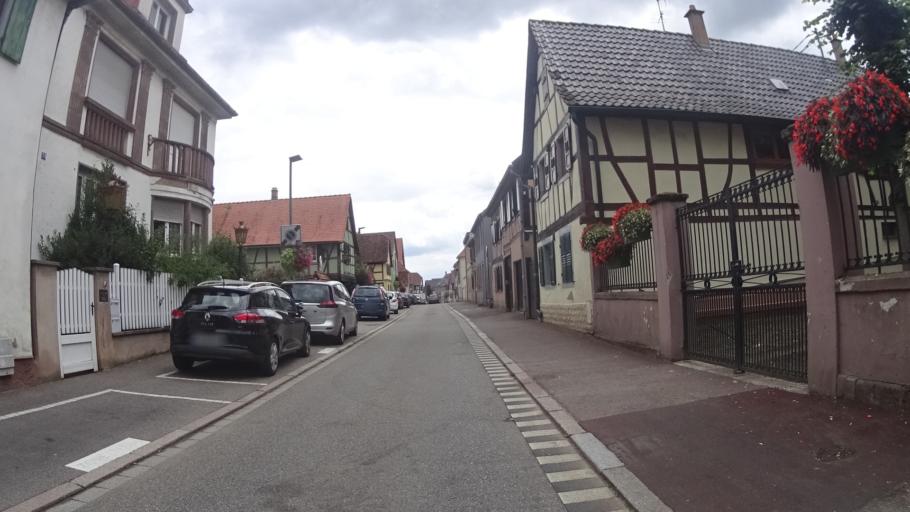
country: FR
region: Alsace
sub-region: Departement du Bas-Rhin
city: Brumath
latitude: 48.7293
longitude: 7.7140
